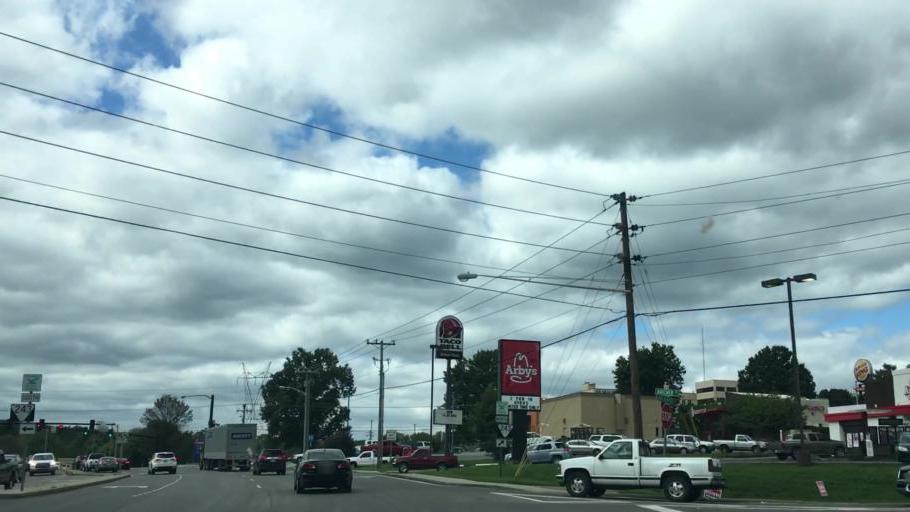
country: US
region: Tennessee
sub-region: Maury County
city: Columbia
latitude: 35.6039
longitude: -87.0662
